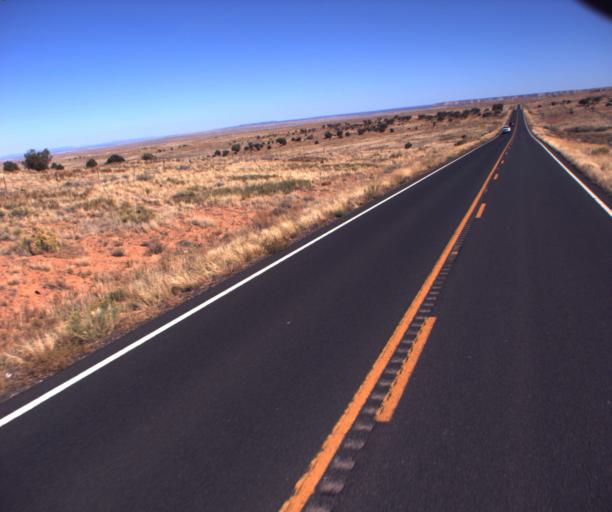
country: US
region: Arizona
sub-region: Apache County
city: Ganado
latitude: 35.7853
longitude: -109.7022
